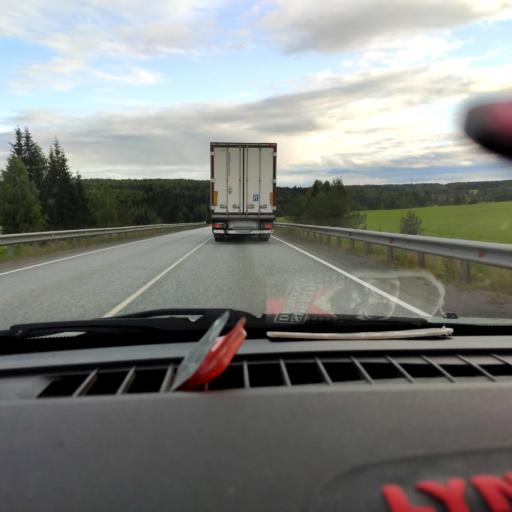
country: RU
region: Perm
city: Pavlovskiy
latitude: 57.9028
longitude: 54.9530
